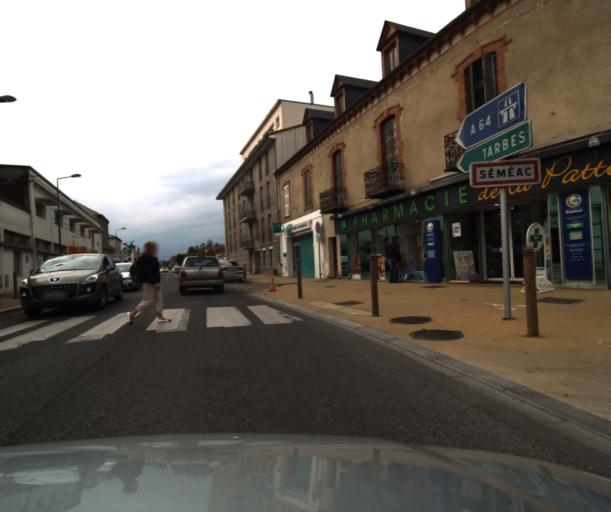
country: FR
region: Midi-Pyrenees
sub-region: Departement des Hautes-Pyrenees
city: Tarbes
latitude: 43.2332
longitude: 0.0920
